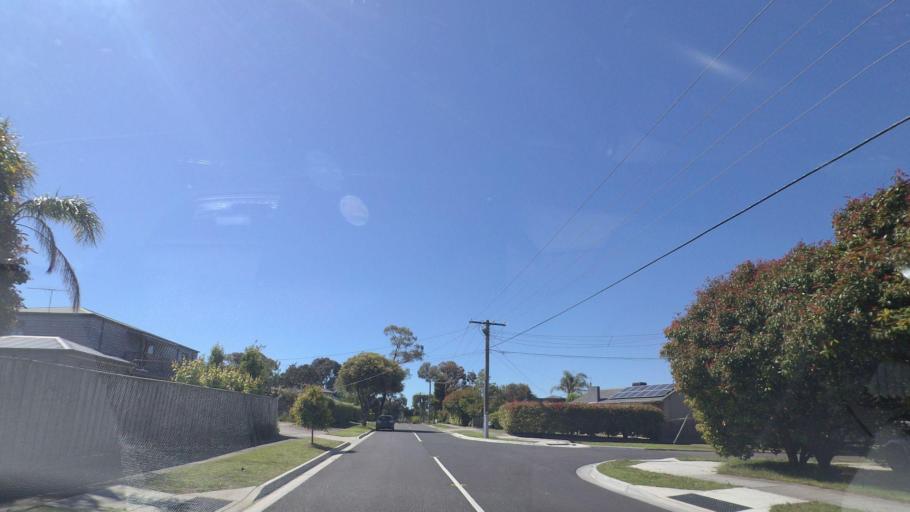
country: AU
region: Victoria
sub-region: Knox
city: Boronia
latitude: -37.8868
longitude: 145.2727
